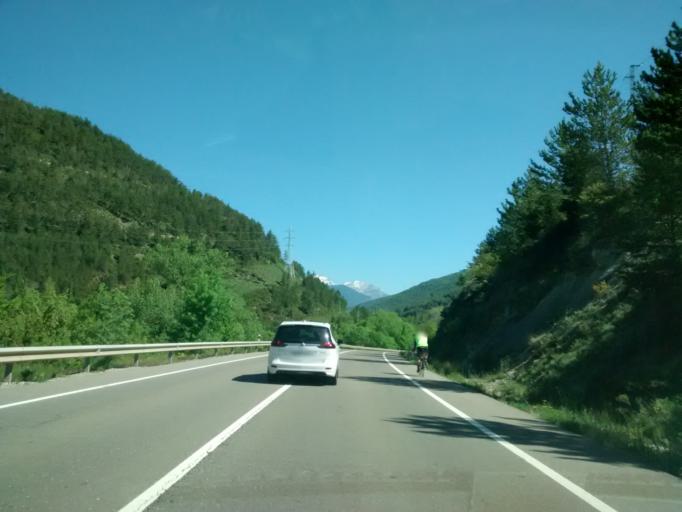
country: ES
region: Aragon
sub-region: Provincia de Huesca
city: Jaca
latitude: 42.5880
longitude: -0.5446
